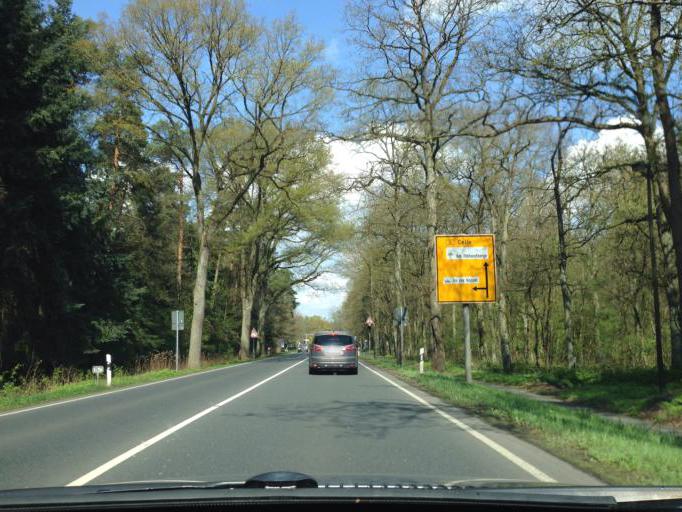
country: DE
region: Lower Saxony
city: Adelheidsdorf
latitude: 52.5874
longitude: 10.0667
